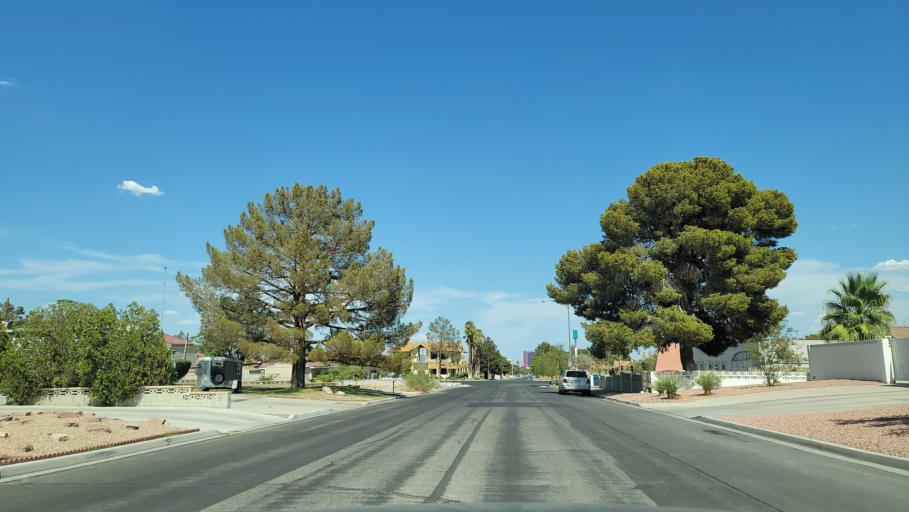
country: US
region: Nevada
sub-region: Clark County
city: Spring Valley
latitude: 36.1349
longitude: -115.2449
